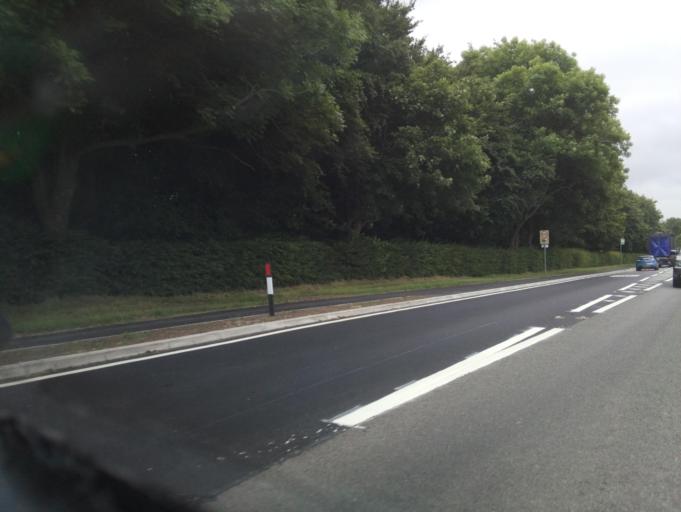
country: GB
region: England
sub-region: Derbyshire
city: Yeldersley
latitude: 52.9754
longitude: -1.6489
